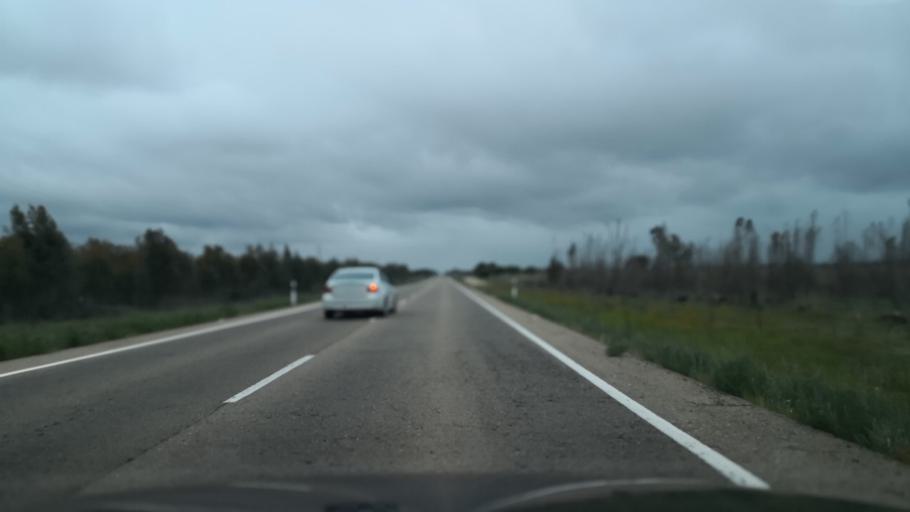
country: ES
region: Extremadura
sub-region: Provincia de Badajoz
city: Badajoz
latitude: 38.9786
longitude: -6.8862
